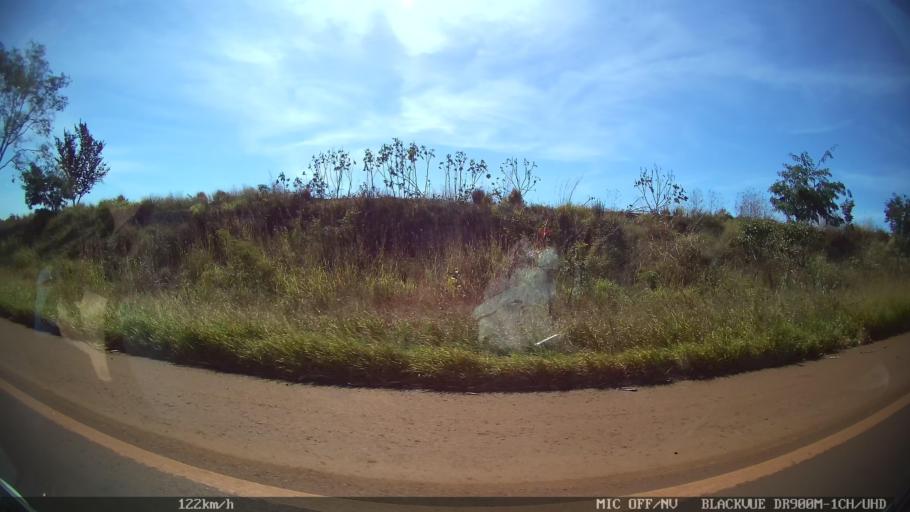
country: BR
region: Sao Paulo
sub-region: Sao Joaquim Da Barra
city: Sao Joaquim da Barra
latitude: -20.5548
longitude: -47.7201
